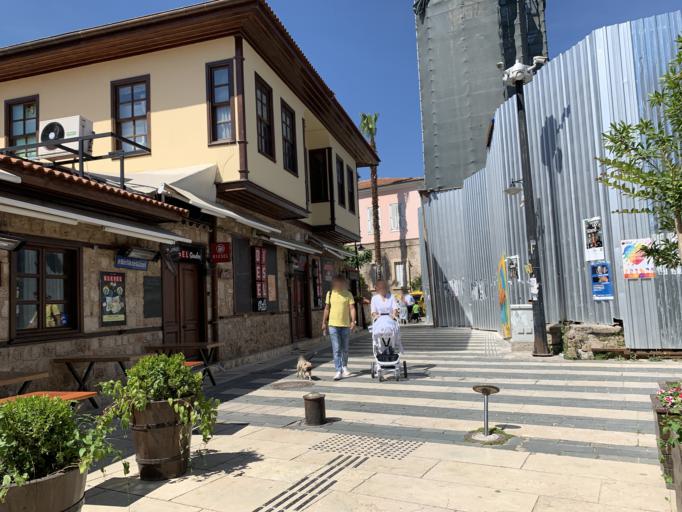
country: TR
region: Antalya
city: Antalya
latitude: 36.8826
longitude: 30.7056
